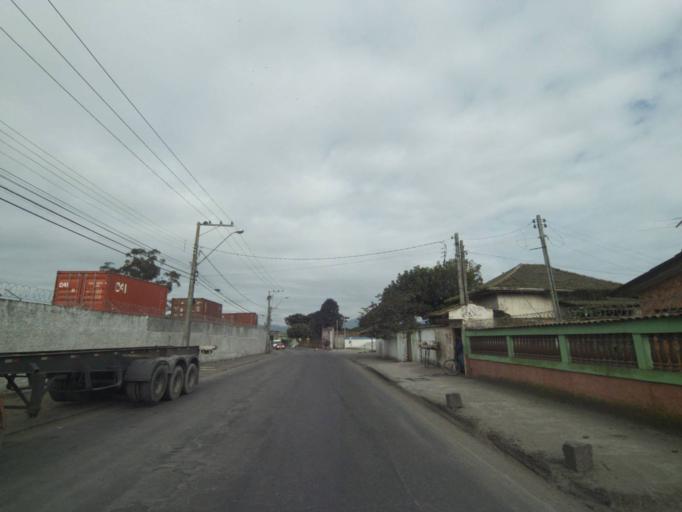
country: BR
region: Parana
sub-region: Paranagua
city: Paranagua
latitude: -25.5151
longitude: -48.5281
